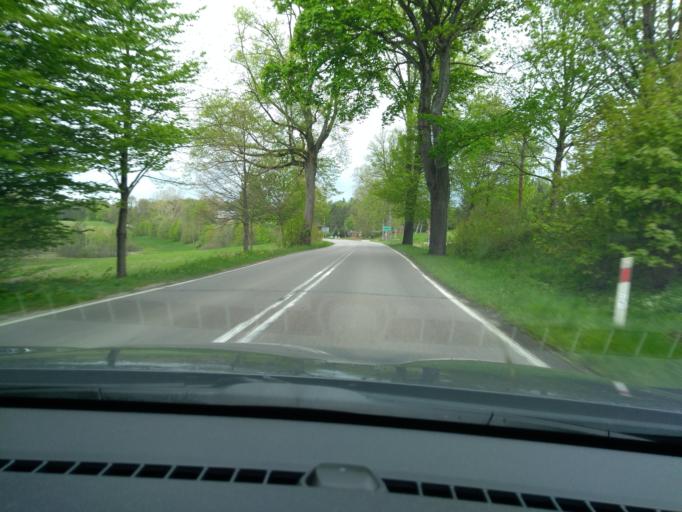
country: PL
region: Pomeranian Voivodeship
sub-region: Powiat kartuski
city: Sierakowice
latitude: 54.3420
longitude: 17.9450
